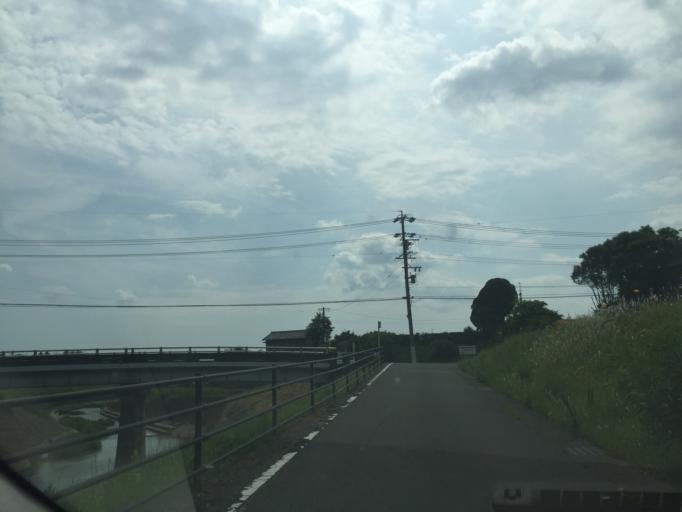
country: JP
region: Shizuoka
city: Kakegawa
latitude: 34.7775
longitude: 138.0364
